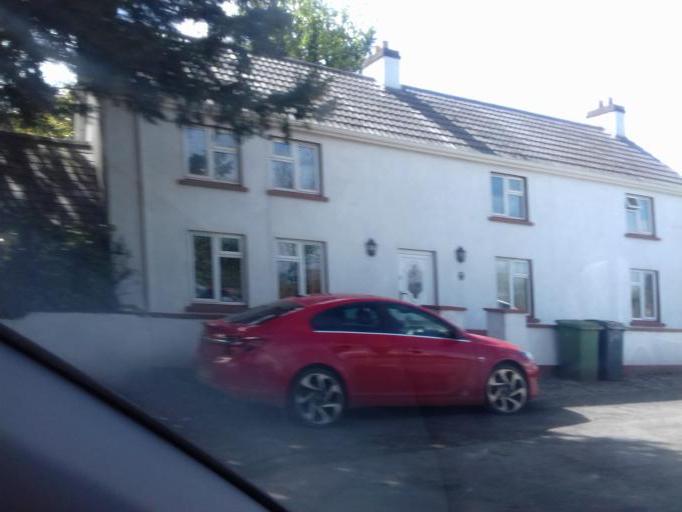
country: GB
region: Northern Ireland
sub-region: Fermanagh District
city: Enniskillen
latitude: 54.3679
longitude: -7.6806
